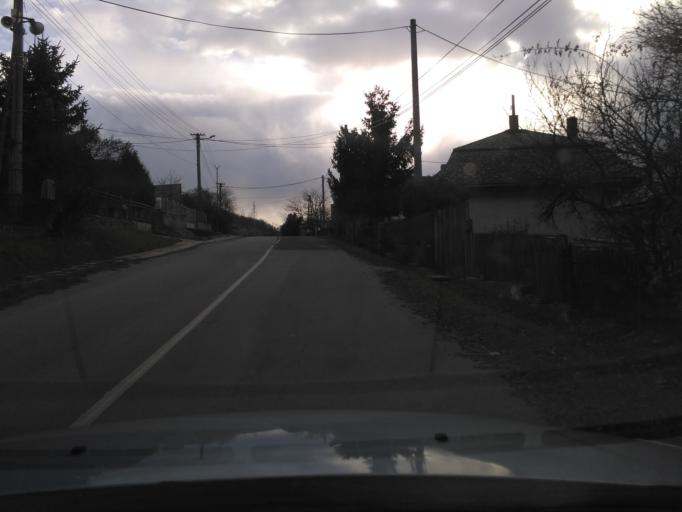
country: HU
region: Borsod-Abauj-Zemplen
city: Satoraljaujhely
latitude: 48.4212
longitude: 21.7273
